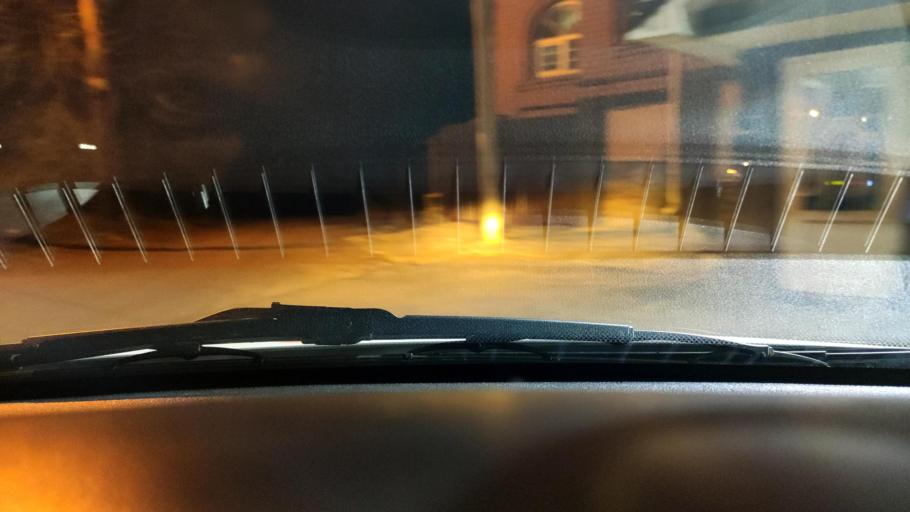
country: RU
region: Voronezj
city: Maslovka
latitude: 51.6041
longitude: 39.2359
